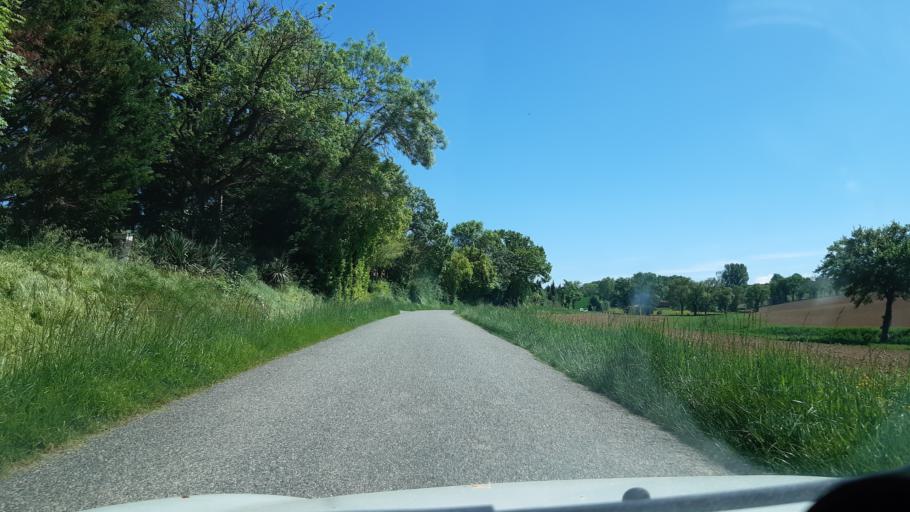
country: FR
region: Midi-Pyrenees
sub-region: Departement du Gers
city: Samatan
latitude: 43.5245
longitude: 0.9870
